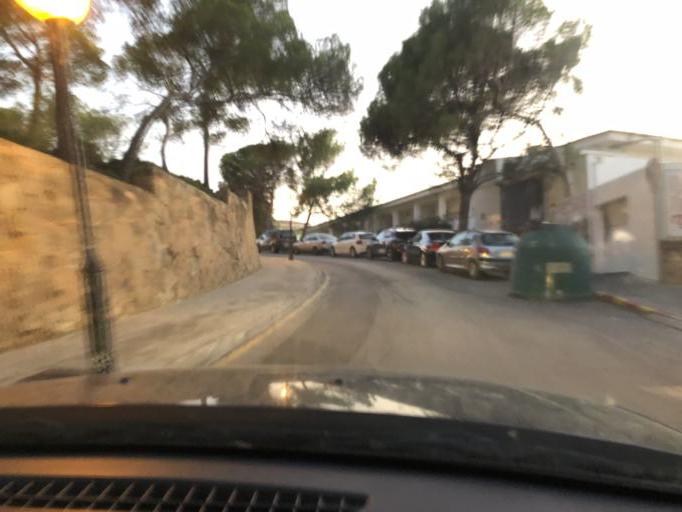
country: ES
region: Balearic Islands
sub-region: Illes Balears
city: Santa Ponsa
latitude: 39.5205
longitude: 2.4679
